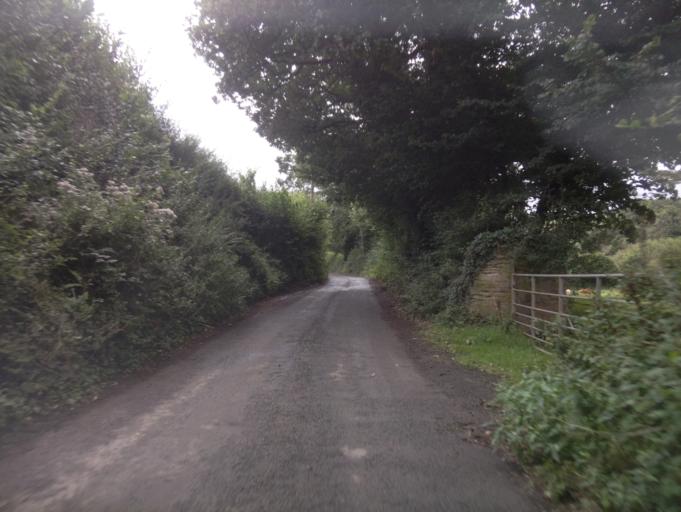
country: GB
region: England
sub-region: Devon
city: Kingsbridge
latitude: 50.2740
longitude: -3.7200
